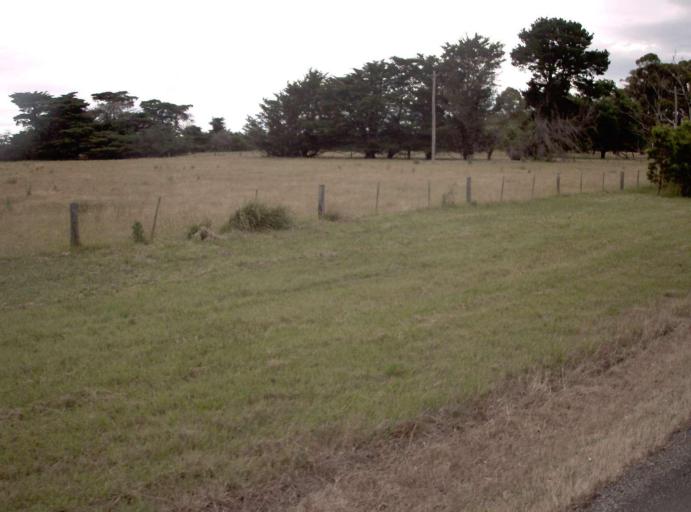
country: AU
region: Victoria
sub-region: Wellington
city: Sale
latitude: -38.3771
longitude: 146.9829
